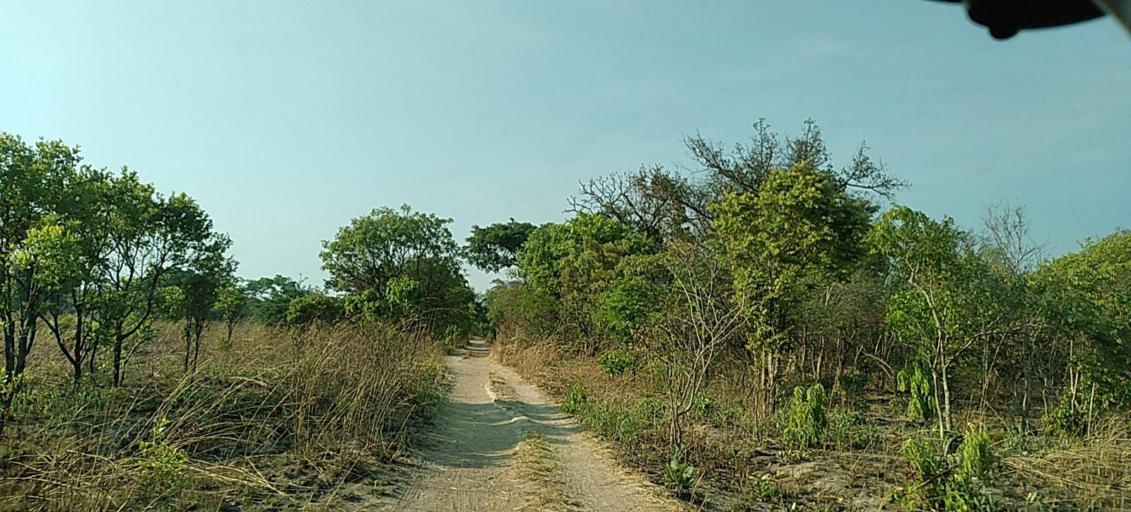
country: ZM
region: North-Western
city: Kalengwa
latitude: -13.1676
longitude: 25.0358
